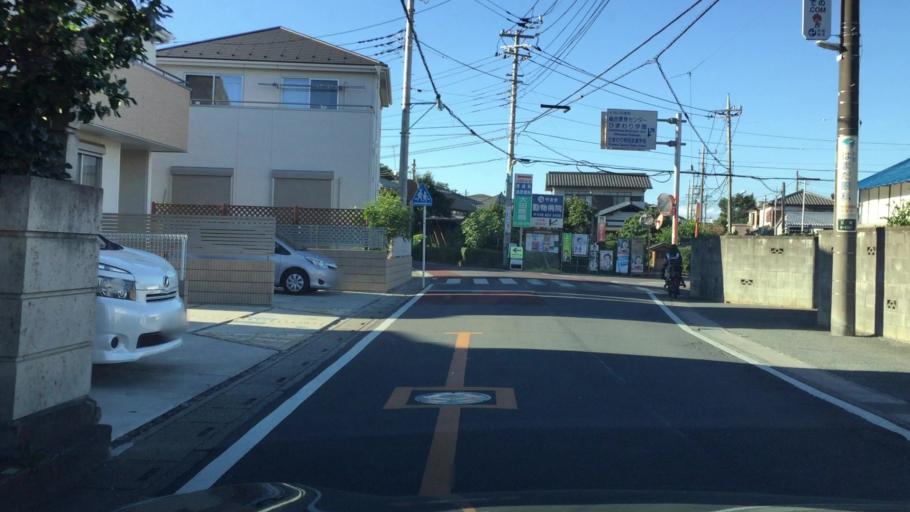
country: JP
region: Saitama
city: Yono
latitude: 35.9182
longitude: 139.5885
